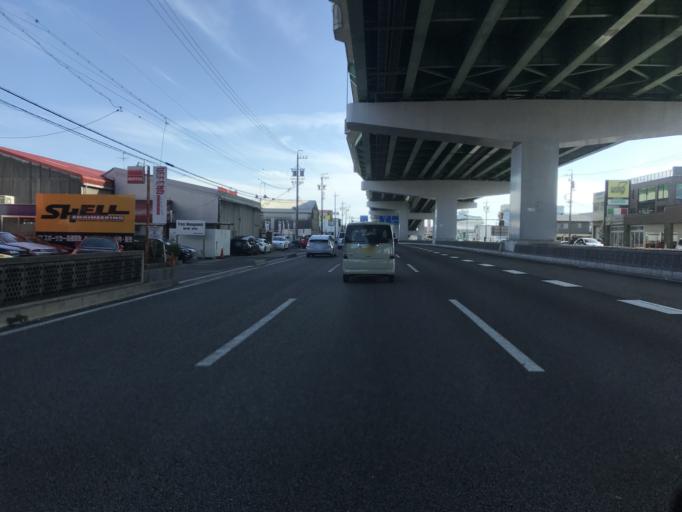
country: JP
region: Aichi
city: Iwakura
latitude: 35.2342
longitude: 136.8497
